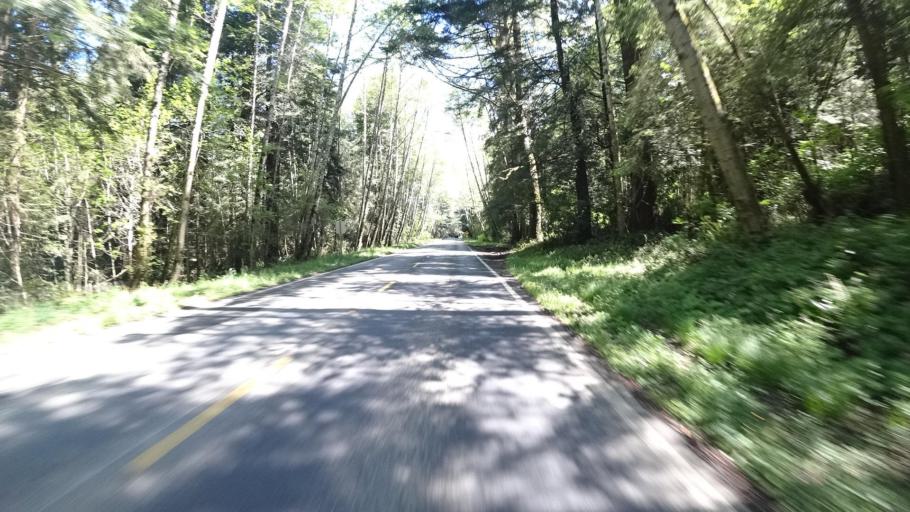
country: US
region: California
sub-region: Humboldt County
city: McKinleyville
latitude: 40.9683
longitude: -124.0669
